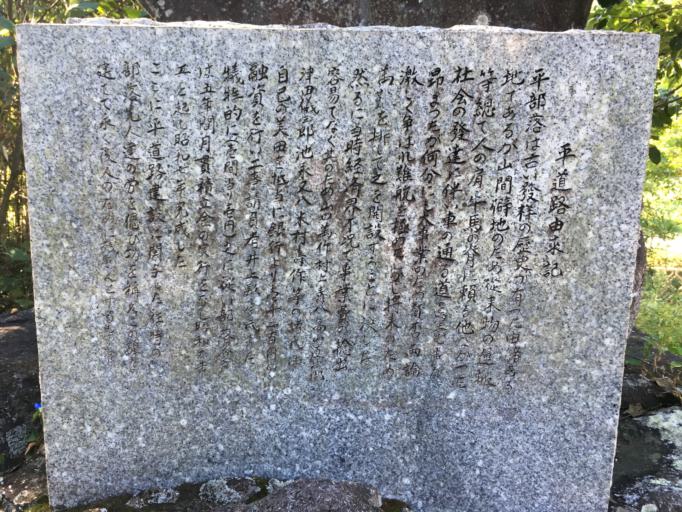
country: JP
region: Kumamoto
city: Kumamoto
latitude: 32.7980
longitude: 130.6607
